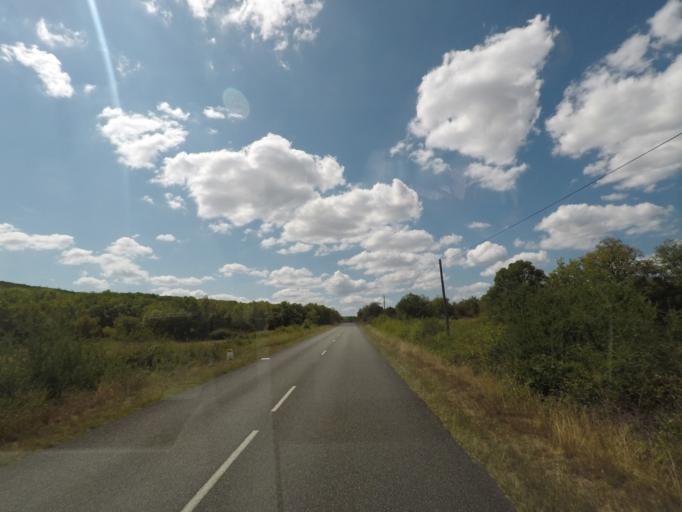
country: FR
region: Midi-Pyrenees
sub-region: Departement du Lot
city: Cajarc
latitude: 44.5857
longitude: 1.7123
